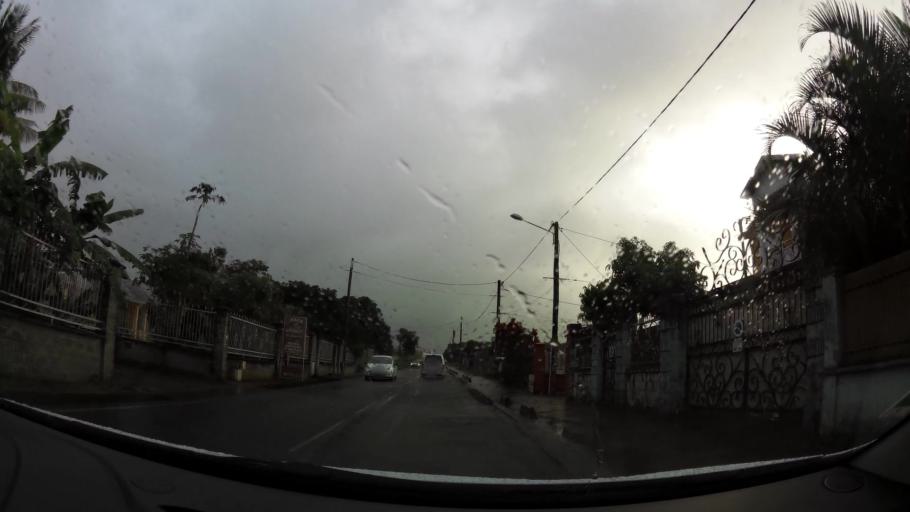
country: RE
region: Reunion
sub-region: Reunion
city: Saint-Andre
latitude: -20.9584
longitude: 55.6647
